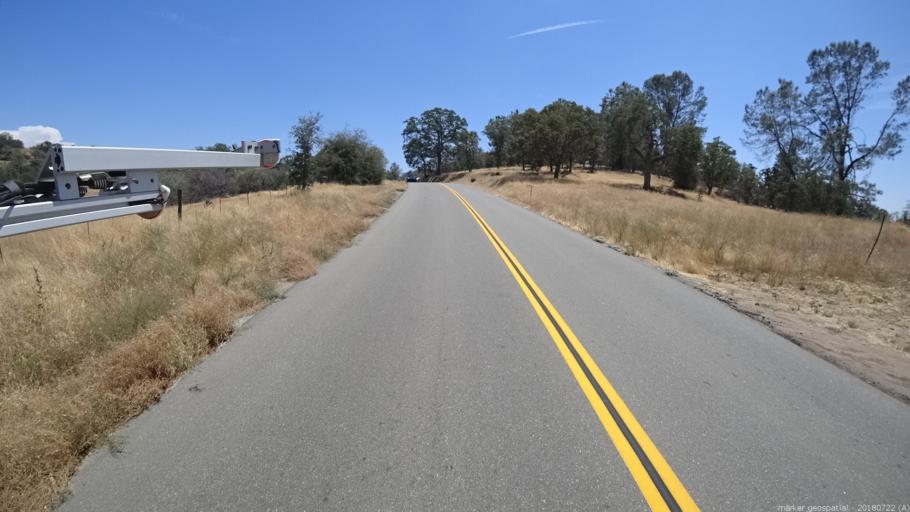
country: US
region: California
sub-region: Madera County
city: Coarsegold
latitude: 37.2277
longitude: -119.7371
